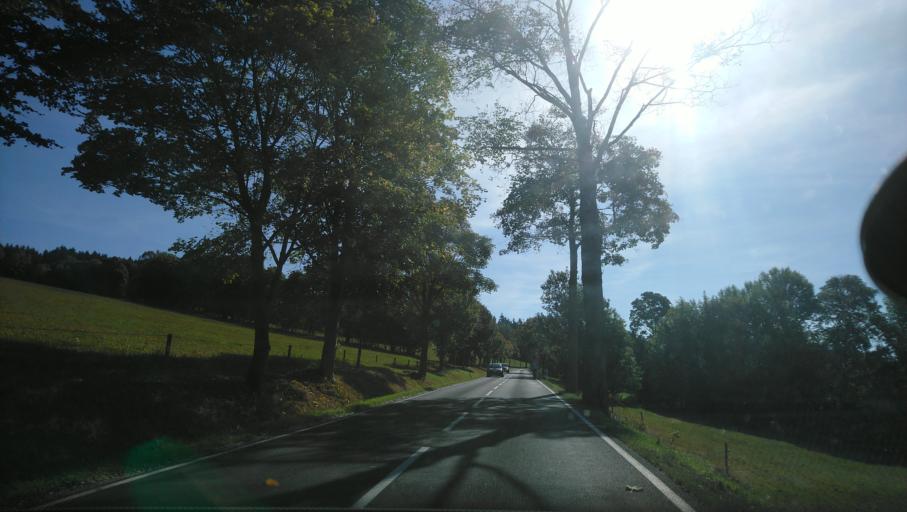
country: DE
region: Saxony
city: Konigswalde
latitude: 50.5340
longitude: 13.0592
